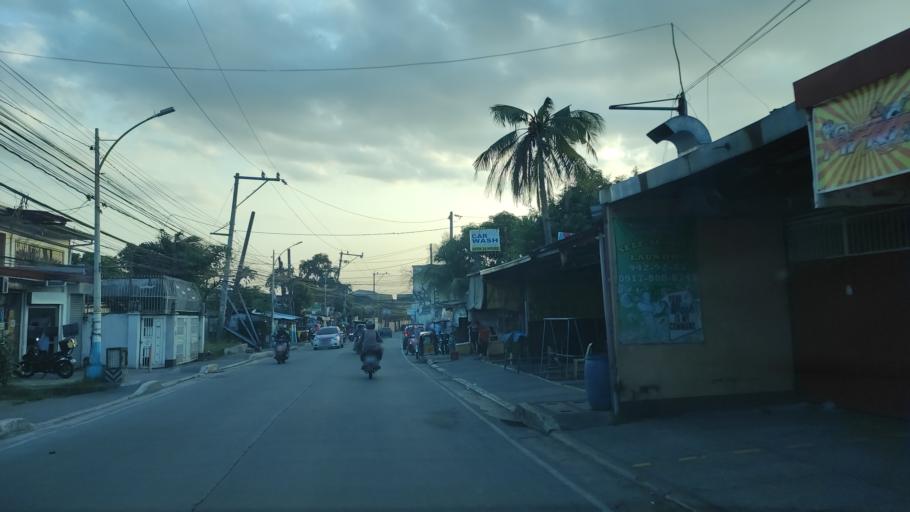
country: PH
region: Calabarzon
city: Bagong Pagasa
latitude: 14.6702
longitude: 121.0253
